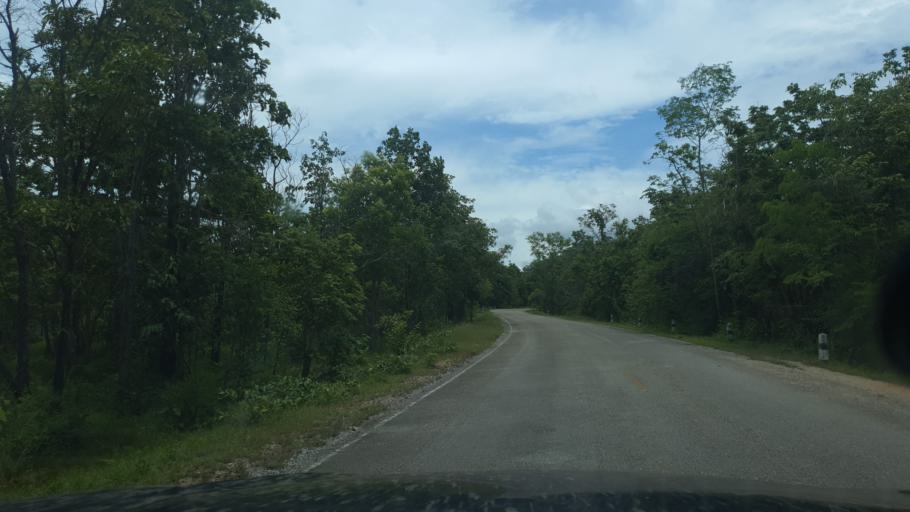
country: TH
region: Lampang
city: Soem Ngam
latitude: 18.0399
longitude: 99.3720
